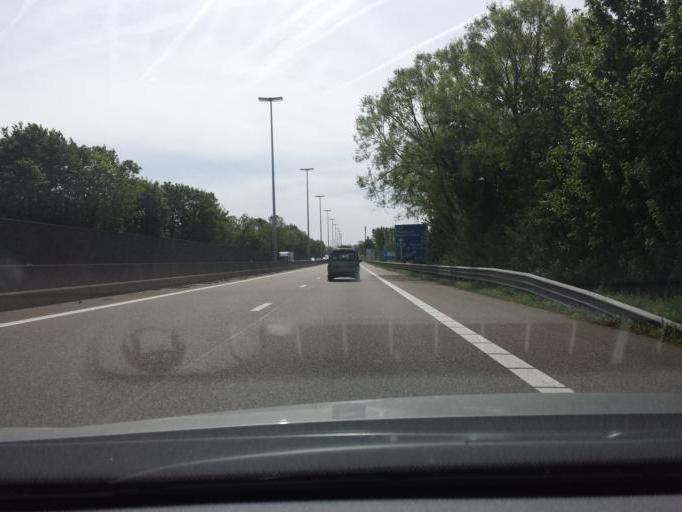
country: BE
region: Flanders
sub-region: Provincie Limburg
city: Hasselt
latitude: 50.9234
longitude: 5.3132
